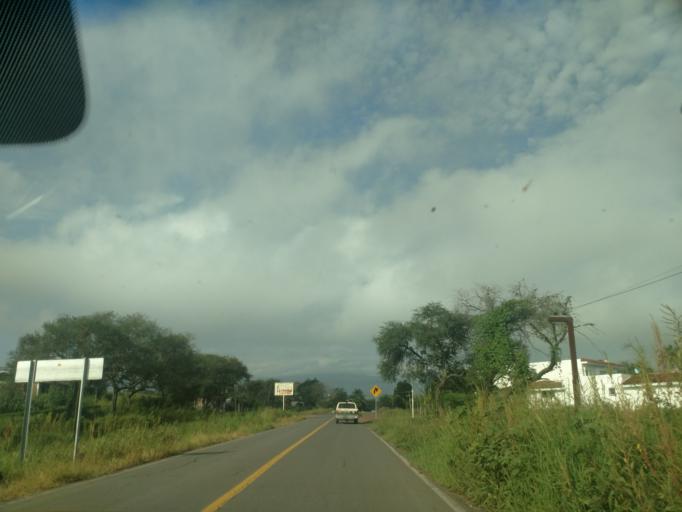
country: MX
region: Jalisco
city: Ameca
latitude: 20.5362
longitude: -104.0505
